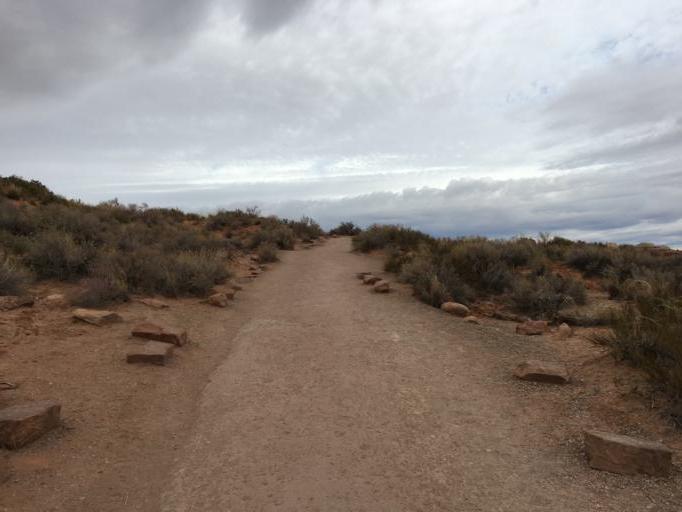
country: US
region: Utah
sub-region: Grand County
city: Moab
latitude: 38.7892
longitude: -109.6019
